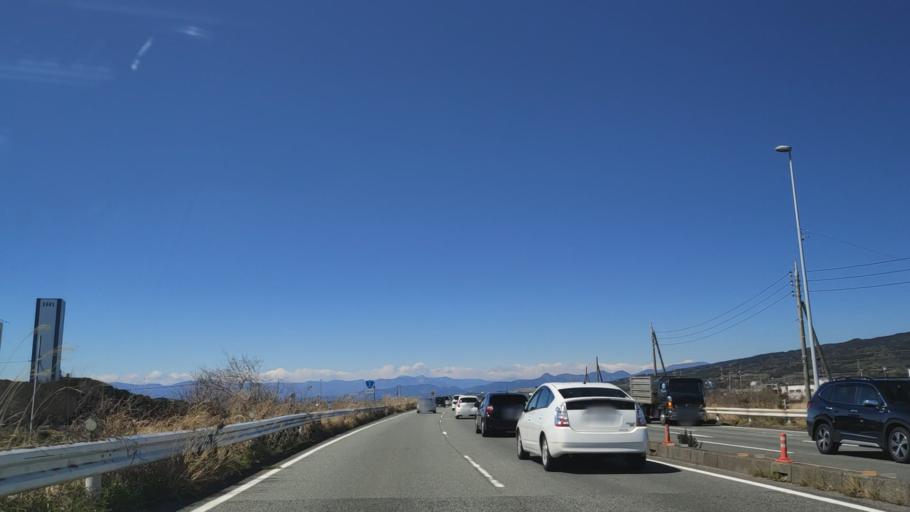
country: JP
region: Shizuoka
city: Numazu
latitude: 35.1315
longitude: 138.7889
